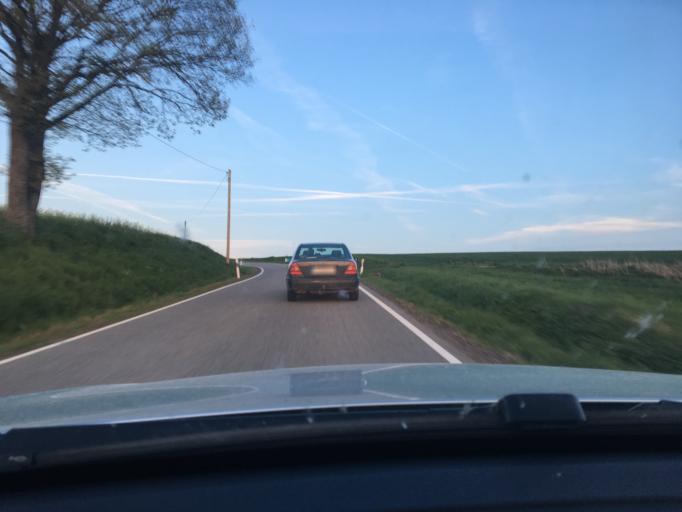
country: DE
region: Rheinland-Pfalz
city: Kriegsfeld
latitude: 49.7136
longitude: 7.9024
